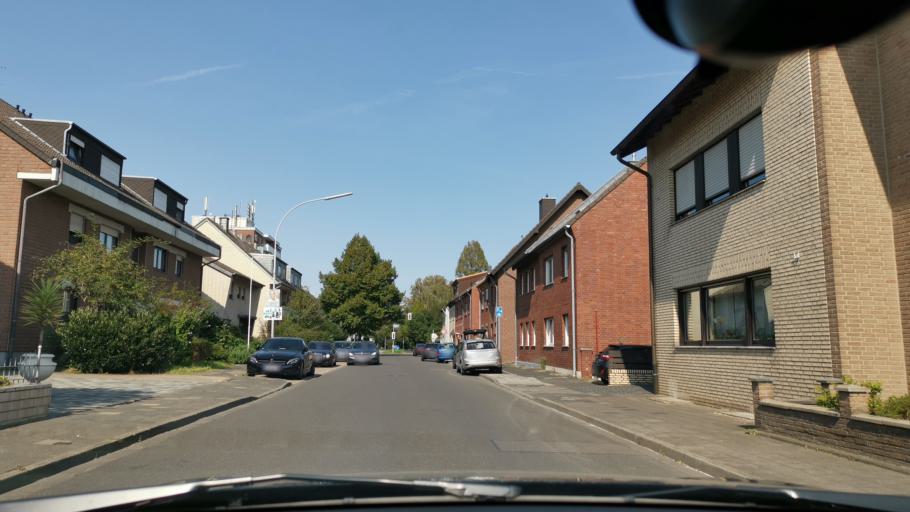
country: DE
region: North Rhine-Westphalia
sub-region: Regierungsbezirk Dusseldorf
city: Grevenbroich
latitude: 51.0756
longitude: 6.5679
